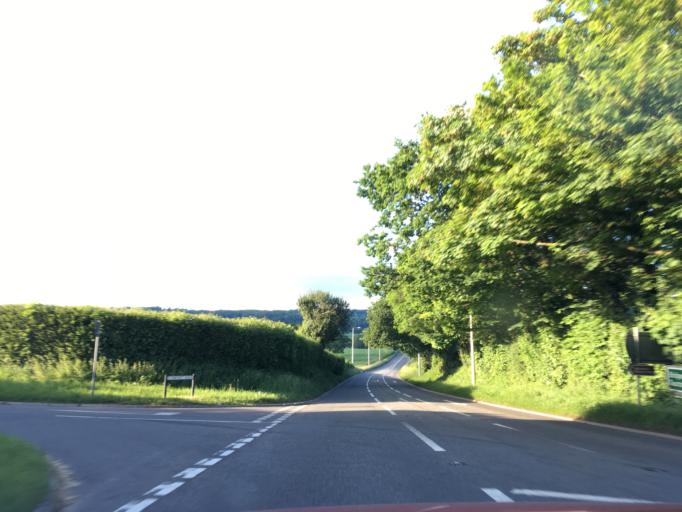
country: GB
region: England
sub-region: North Somerset
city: Burrington
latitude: 51.3460
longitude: -2.7510
